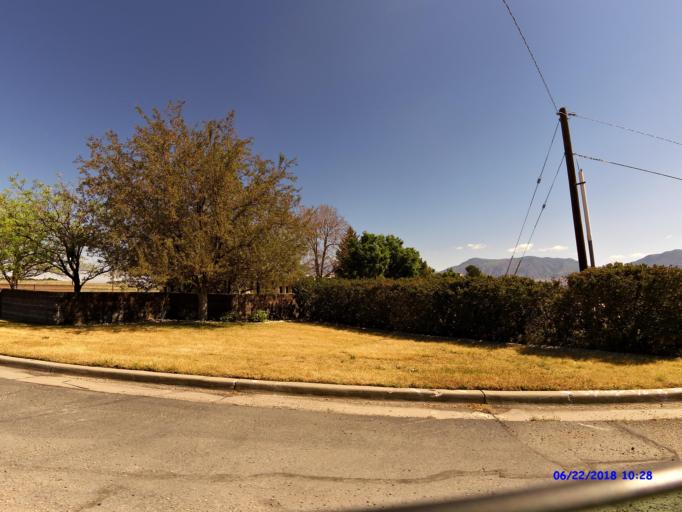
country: US
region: Utah
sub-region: Weber County
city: Riverdale
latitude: 41.1835
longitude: -112.0138
